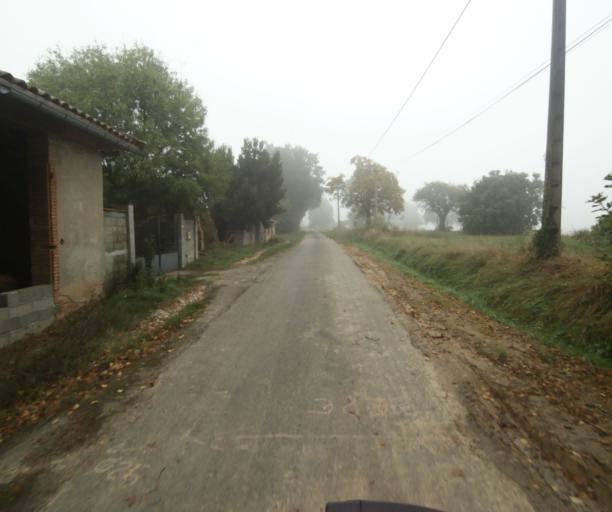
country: FR
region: Midi-Pyrenees
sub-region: Departement du Tarn-et-Garonne
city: Nohic
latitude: 43.9105
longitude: 1.4691
